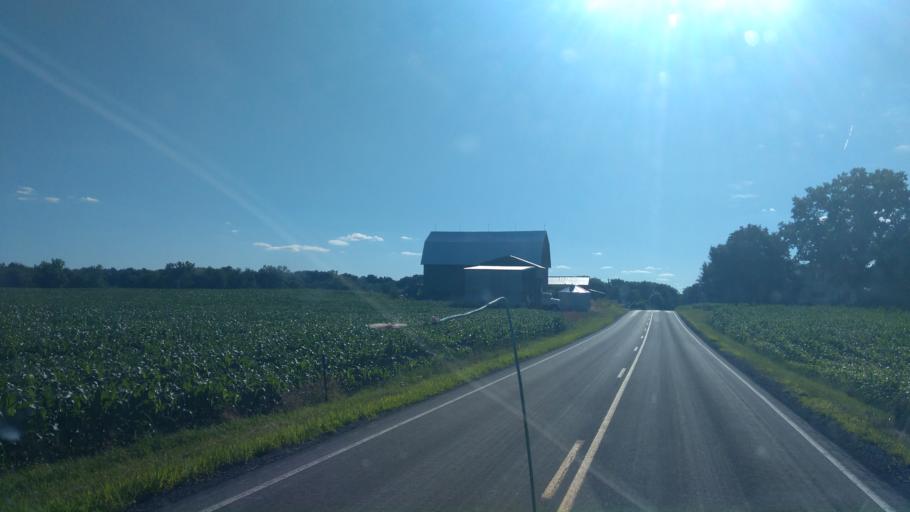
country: US
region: New York
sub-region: Wayne County
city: Clyde
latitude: 43.0011
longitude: -76.8906
